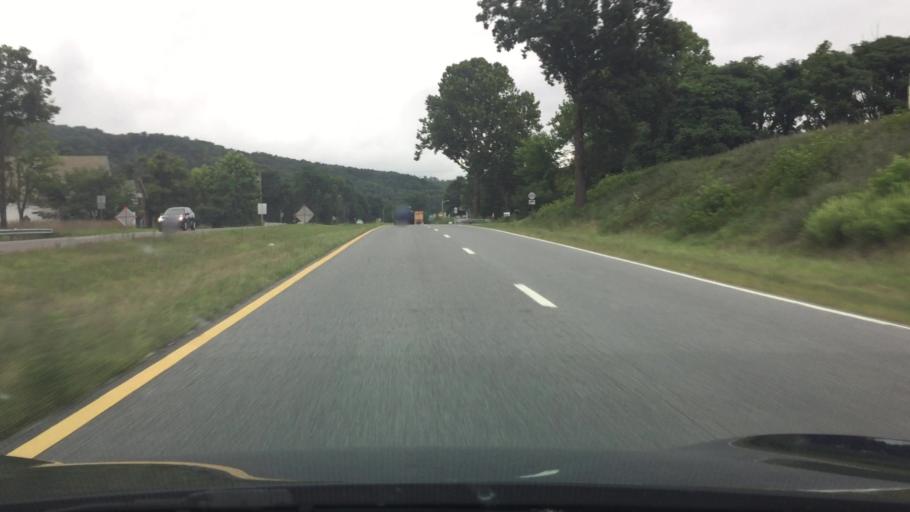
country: US
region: Virginia
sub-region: Montgomery County
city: Shawsville
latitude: 37.2148
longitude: -80.2328
